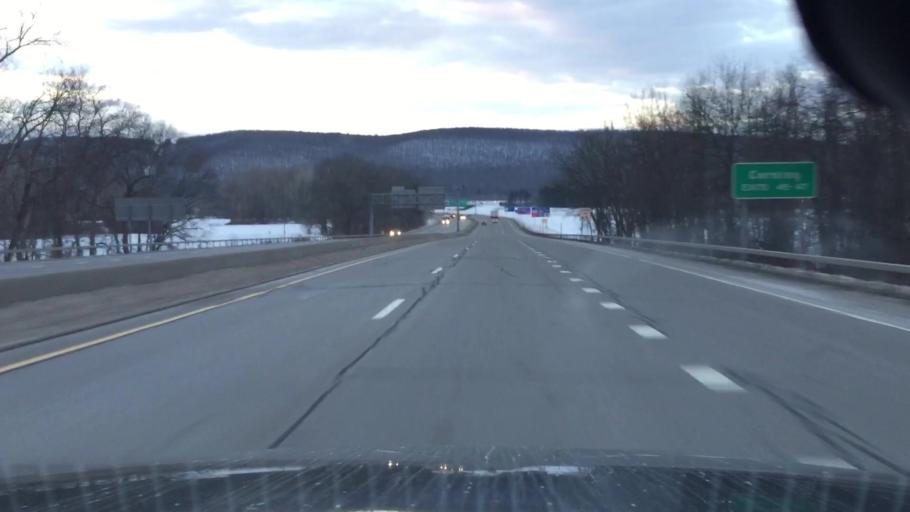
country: US
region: New York
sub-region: Steuben County
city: Painted Post
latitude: 42.1668
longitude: -77.1037
